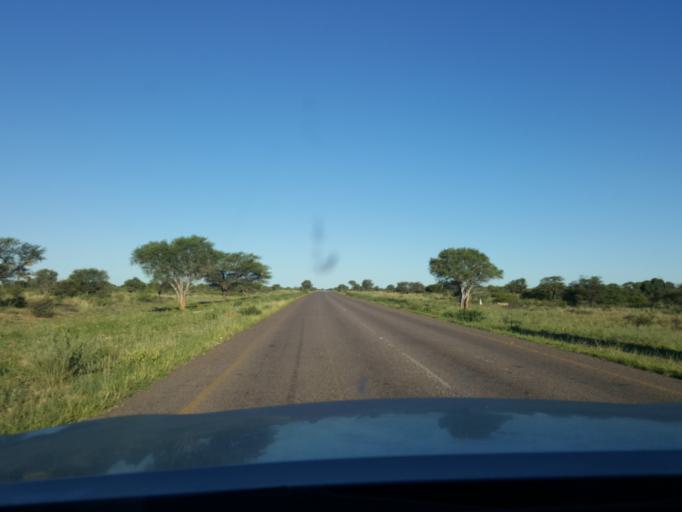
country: BW
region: Southern
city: Khakhea
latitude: -24.3078
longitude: 23.4080
